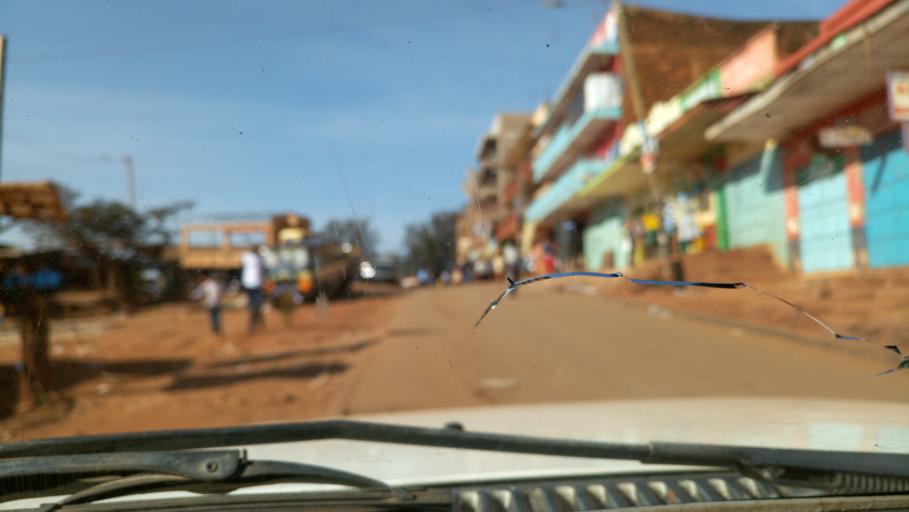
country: KE
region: Murang'a District
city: Murang'a
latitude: -0.7316
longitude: 37.1493
